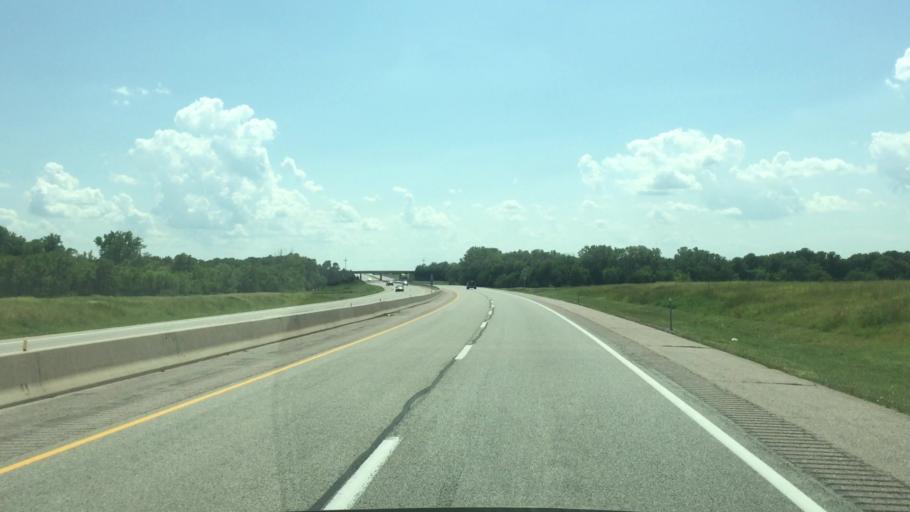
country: US
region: Kansas
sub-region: Butler County
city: El Dorado
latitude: 38.0471
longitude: -96.6406
